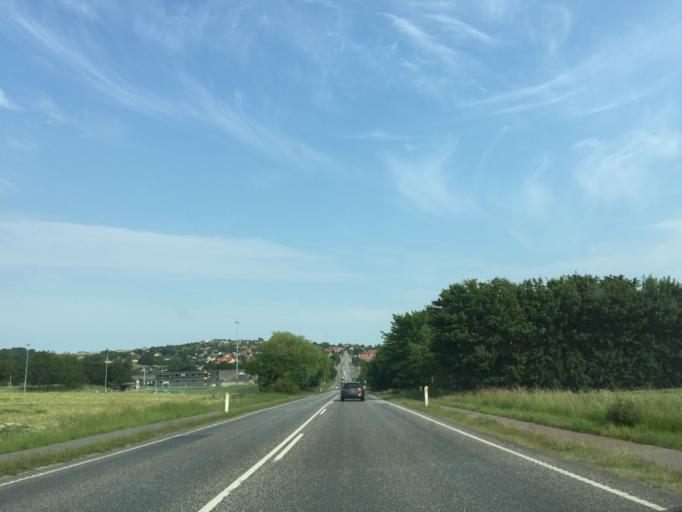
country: DK
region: Central Jutland
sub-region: Syddjurs Kommune
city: Ronde
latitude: 56.3049
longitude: 10.4555
